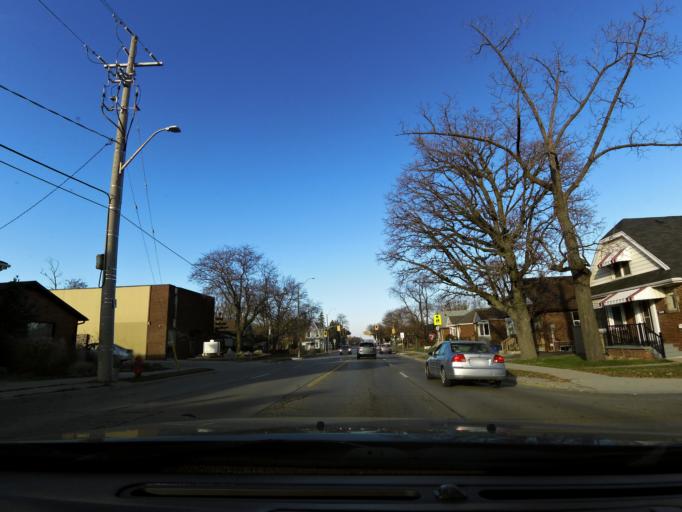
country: CA
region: Ontario
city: Hamilton
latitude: 43.2413
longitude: -79.8762
